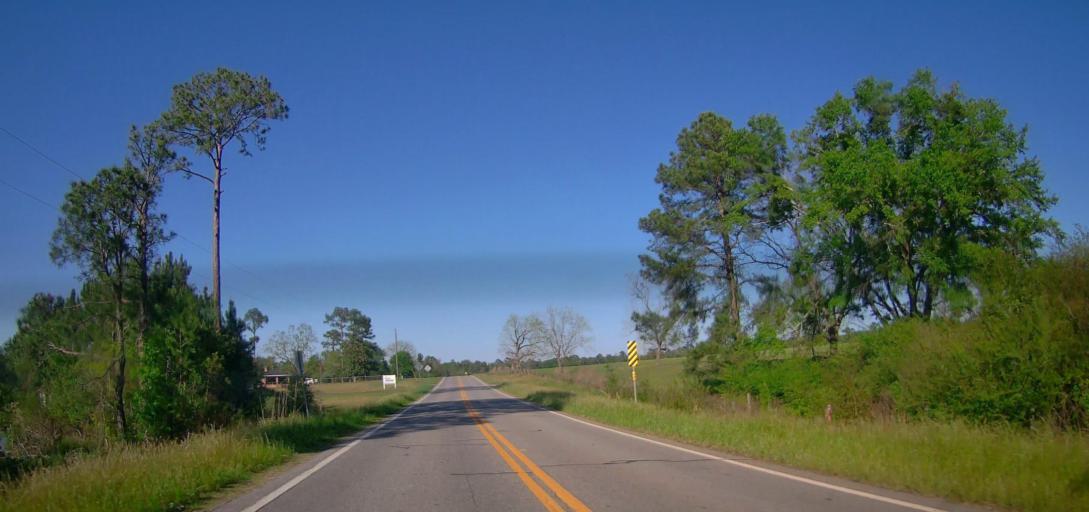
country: US
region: Georgia
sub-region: Wilcox County
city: Rochelle
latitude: 31.9268
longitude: -83.4649
